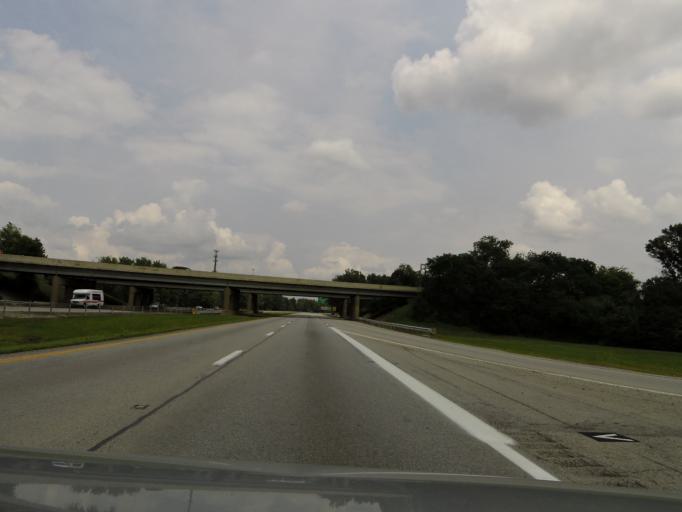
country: US
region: Kentucky
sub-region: Jefferson County
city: Worthington
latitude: 38.3141
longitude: -85.5829
